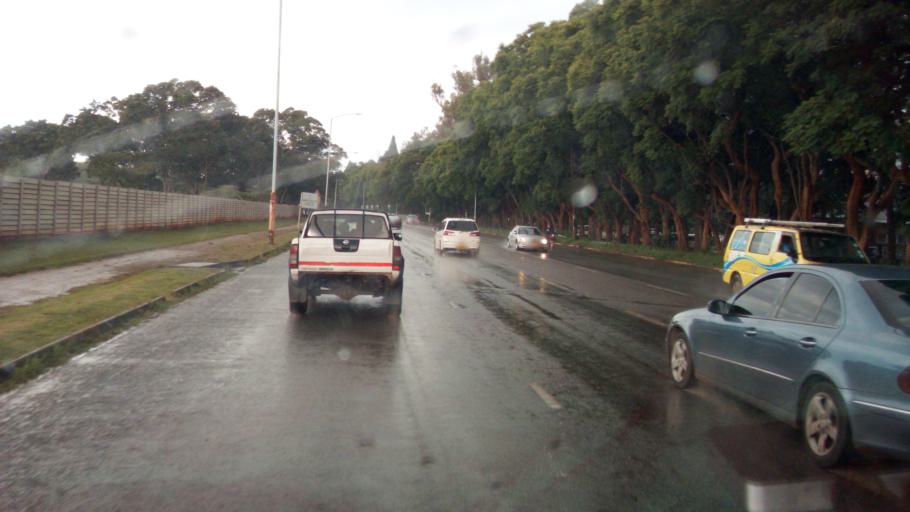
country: ZW
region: Harare
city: Harare
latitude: -17.8077
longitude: 31.0568
